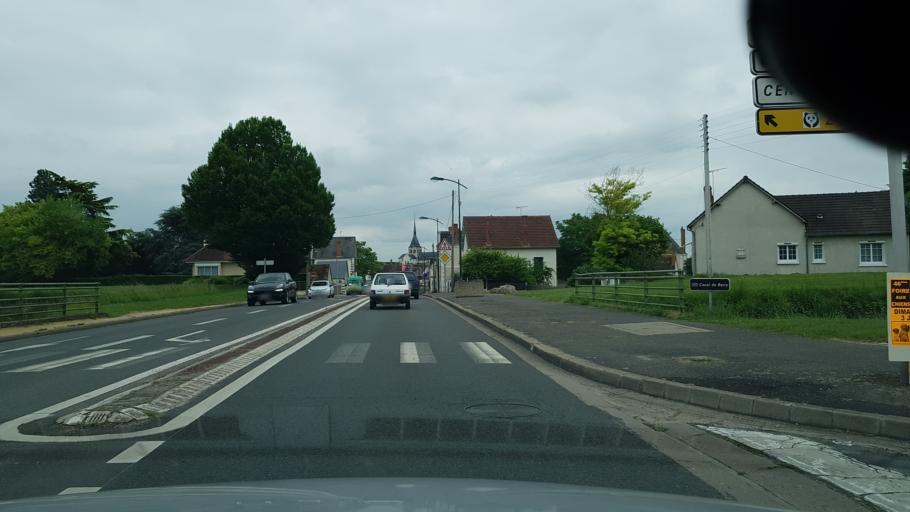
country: FR
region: Centre
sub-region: Departement du Loir-et-Cher
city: Selles-sur-Cher
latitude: 47.2791
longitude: 1.5484
